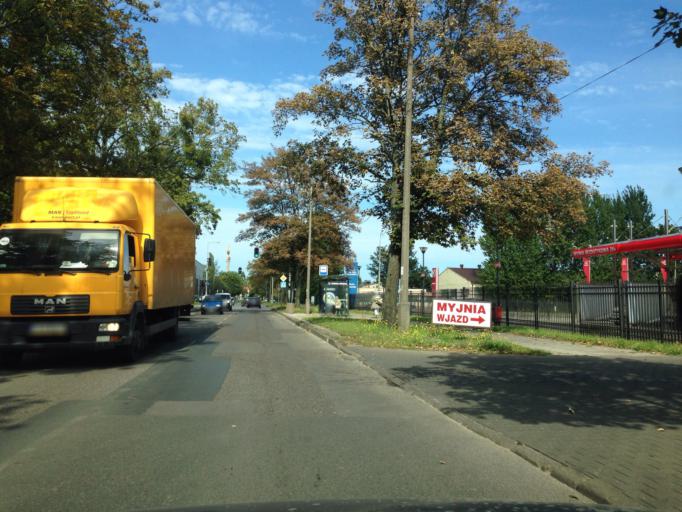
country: PL
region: Pomeranian Voivodeship
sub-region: Gdansk
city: Gdansk
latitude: 54.3938
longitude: 18.6174
